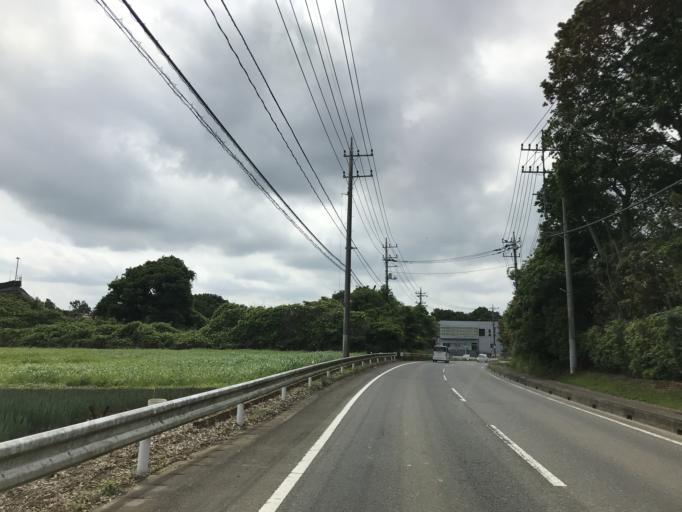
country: JP
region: Ibaraki
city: Ushiku
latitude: 35.9769
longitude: 140.0760
